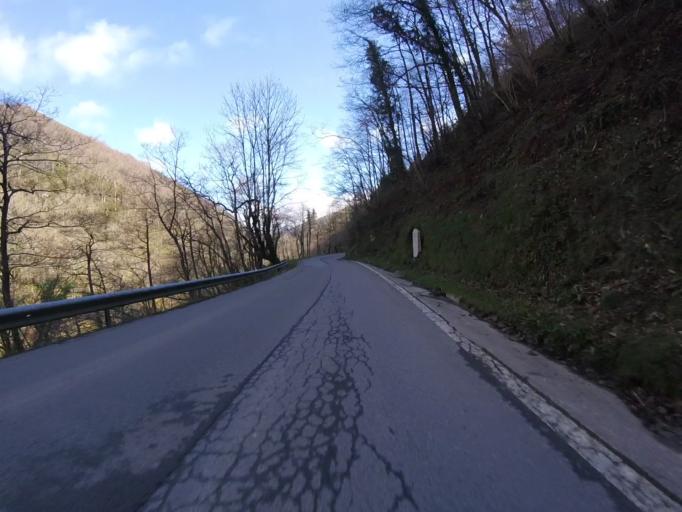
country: ES
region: Navarre
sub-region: Provincia de Navarra
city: Ezkurra
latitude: 43.1028
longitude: -1.8629
